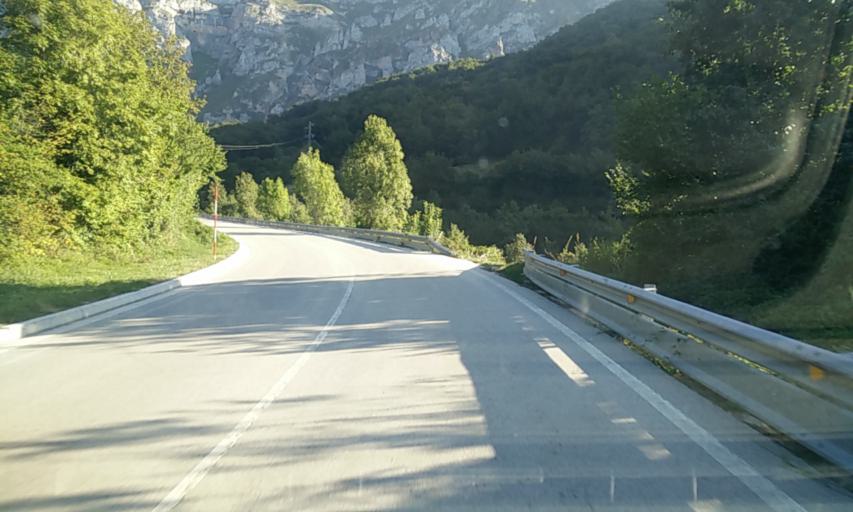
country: ES
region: Castille and Leon
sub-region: Provincia de Leon
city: Posada de Valdeon
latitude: 43.1388
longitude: -4.8099
